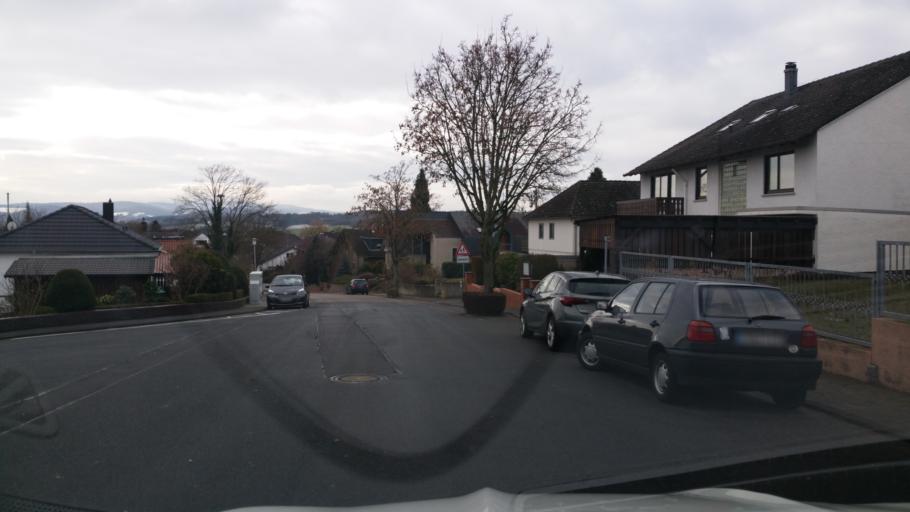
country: DE
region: Hesse
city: Reinheim
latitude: 49.8311
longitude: 8.8236
